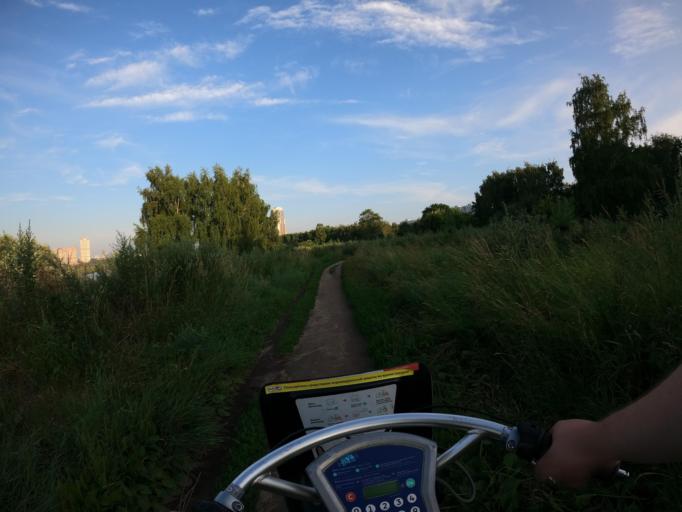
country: RU
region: Moscow
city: Strogino
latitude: 55.8128
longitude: 37.4155
